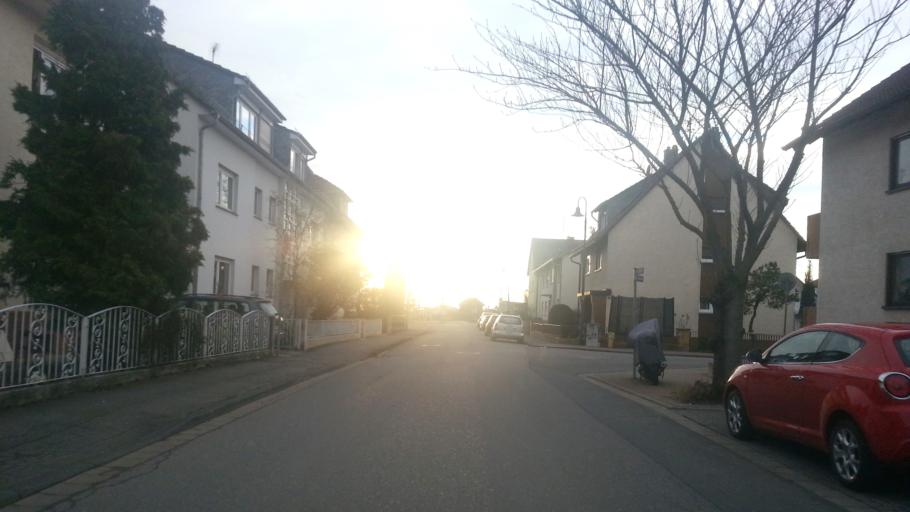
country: DE
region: Baden-Wuerttemberg
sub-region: Karlsruhe Region
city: Edingen-Neckarhausen
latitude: 49.4424
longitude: 8.6157
